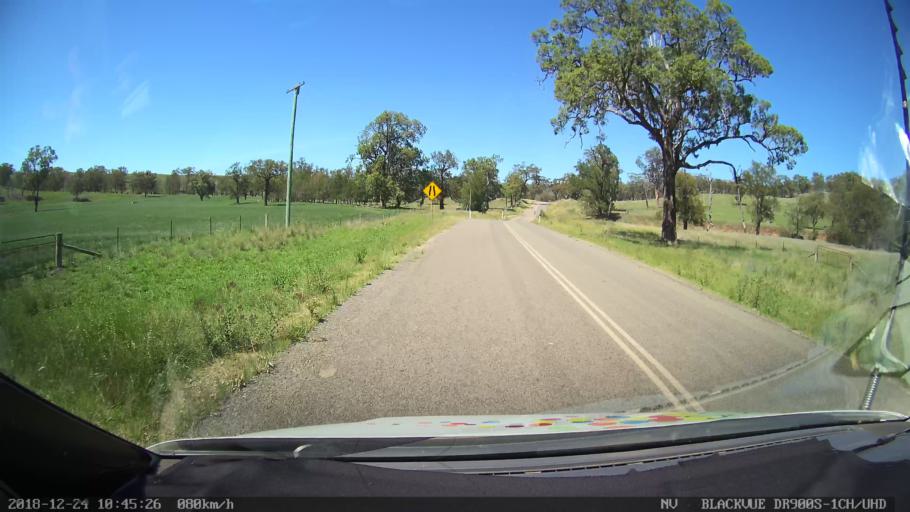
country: AU
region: New South Wales
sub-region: Upper Hunter Shire
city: Merriwa
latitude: -31.9030
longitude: 150.4357
